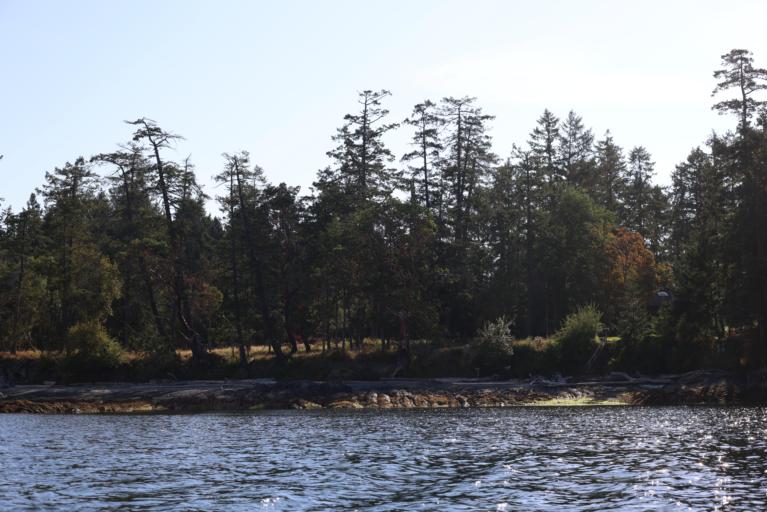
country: CA
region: British Columbia
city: North Saanich
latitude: 48.6897
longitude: -123.4861
